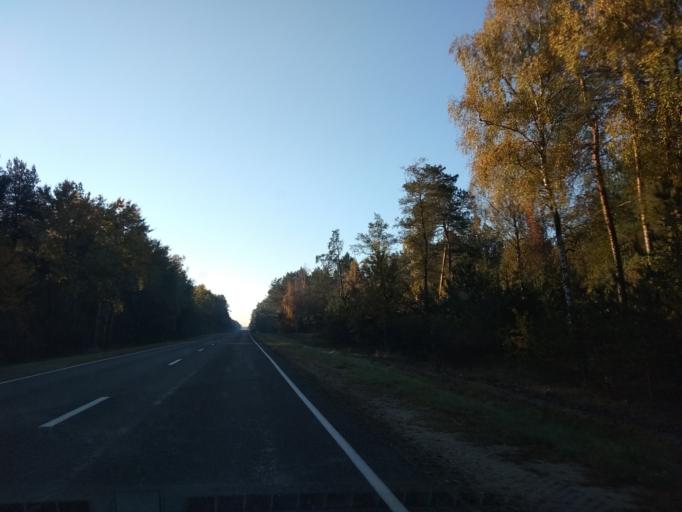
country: BY
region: Brest
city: Kobryn
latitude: 52.0933
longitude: 24.2786
